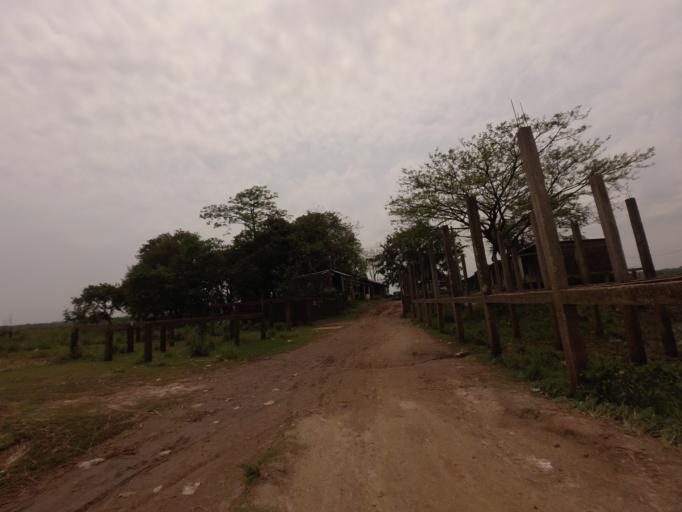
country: BD
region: Sylhet
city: Sylhet
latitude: 25.0067
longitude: 91.9163
